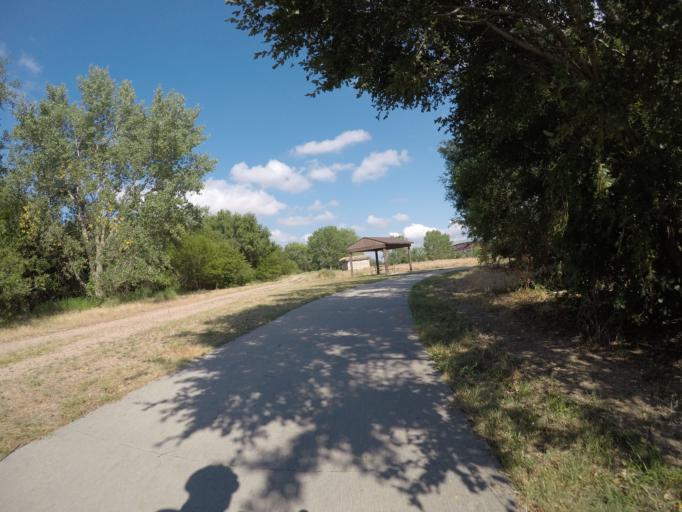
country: US
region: Nebraska
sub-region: Buffalo County
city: Kearney
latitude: 40.6725
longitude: -99.0425
